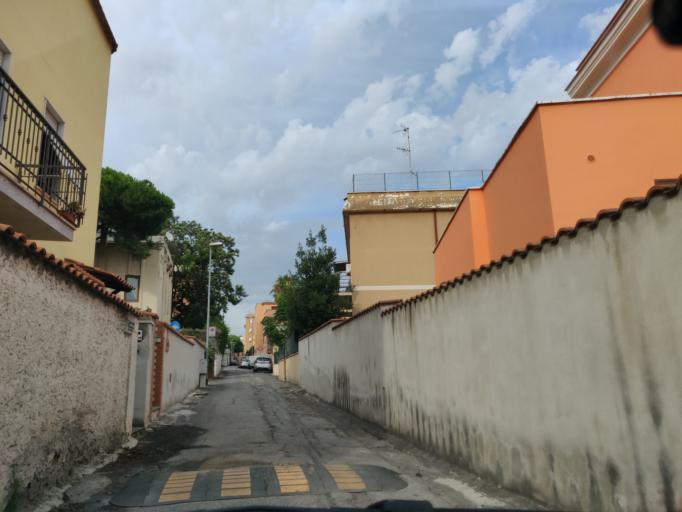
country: IT
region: Latium
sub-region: Citta metropolitana di Roma Capitale
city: Civitavecchia
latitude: 42.0907
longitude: 11.8048
